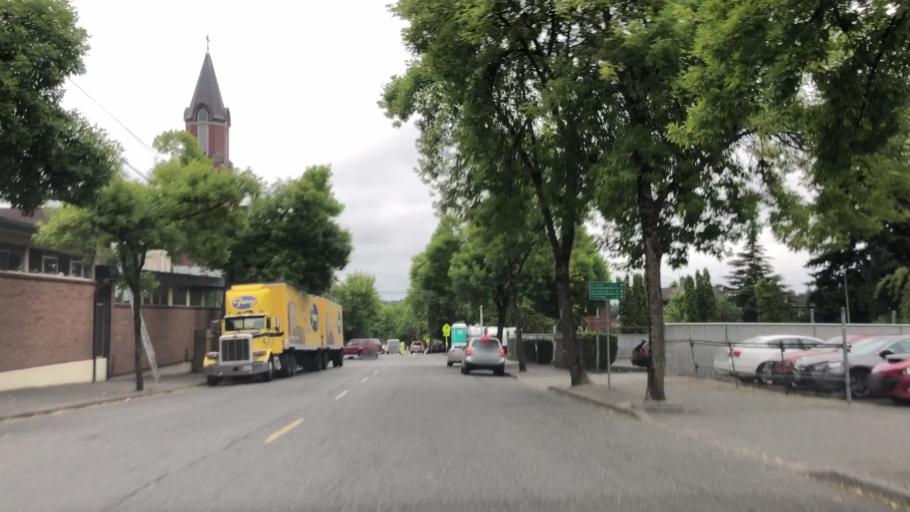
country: US
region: Washington
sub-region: King County
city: Seattle
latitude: 47.5982
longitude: -122.3064
